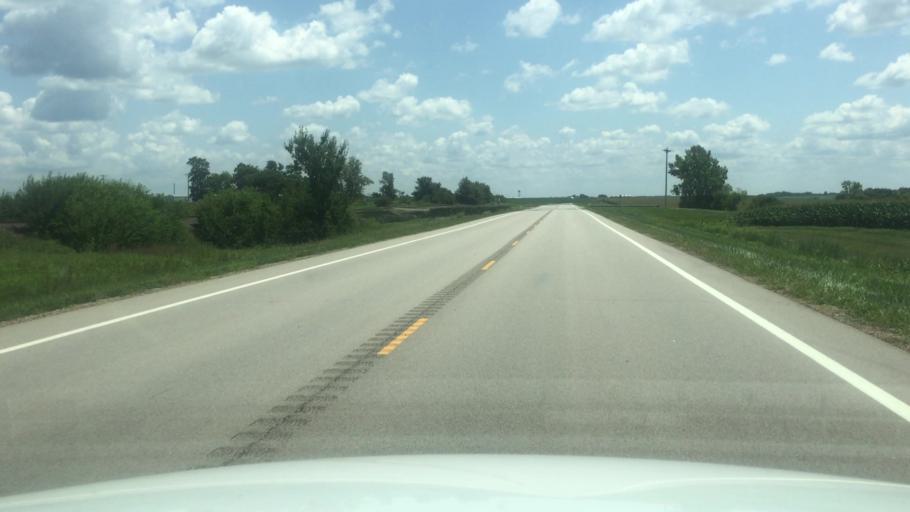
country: US
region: Kansas
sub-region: Brown County
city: Horton
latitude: 39.5962
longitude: -95.3335
